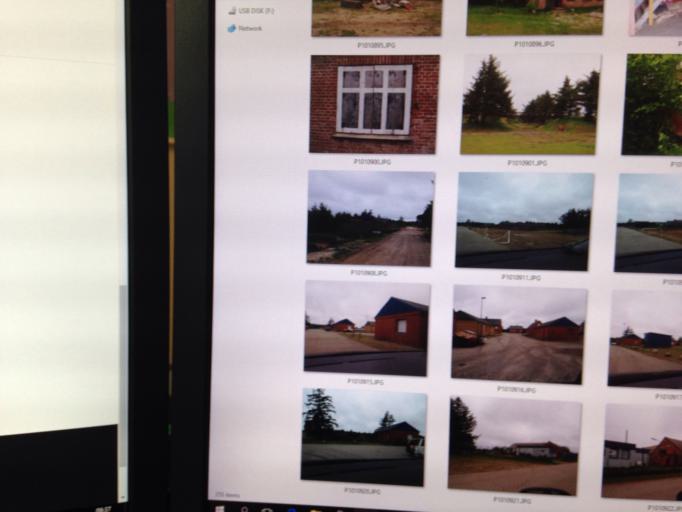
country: DK
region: Central Jutland
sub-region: Skive Kommune
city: Skive
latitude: 56.5430
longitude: 9.0393
